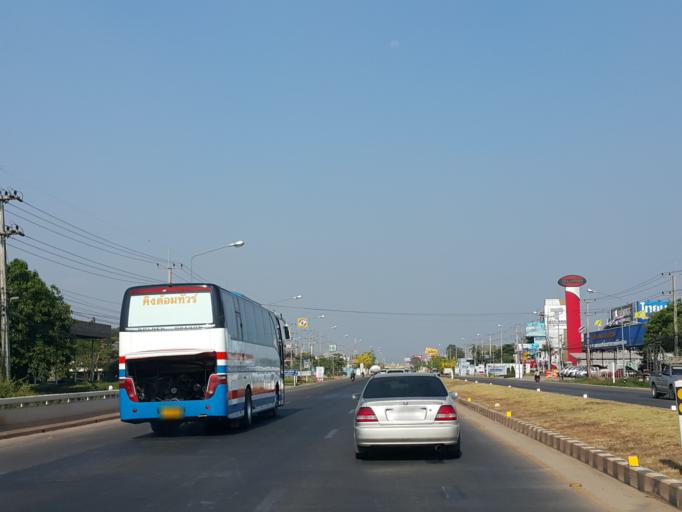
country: TH
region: Phitsanulok
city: Phitsanulok
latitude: 16.8163
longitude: 100.3048
